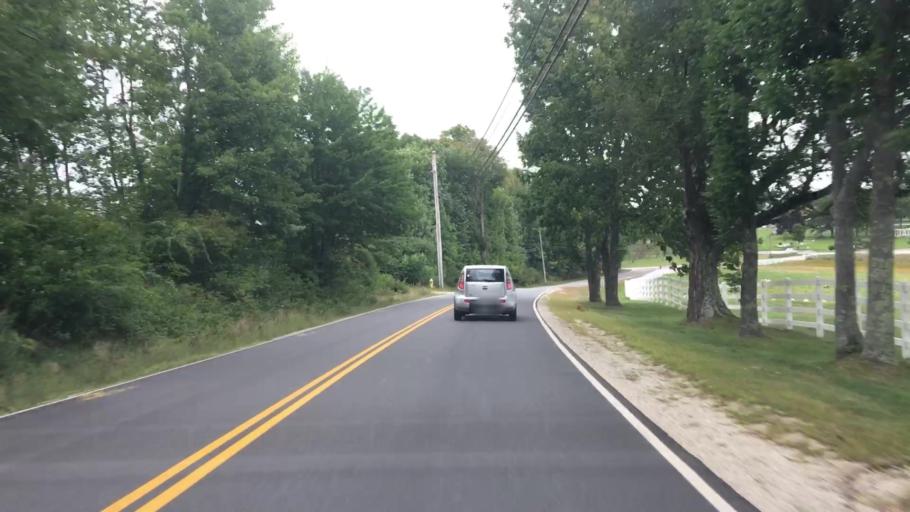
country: US
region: Maine
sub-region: Cumberland County
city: New Gloucester
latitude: 43.8971
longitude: -70.2561
